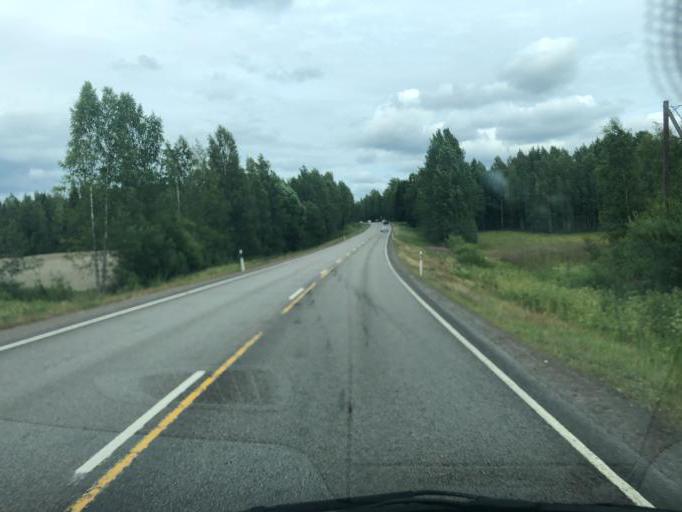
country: FI
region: Kymenlaakso
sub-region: Kouvola
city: Kouvola
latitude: 60.9469
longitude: 26.8380
